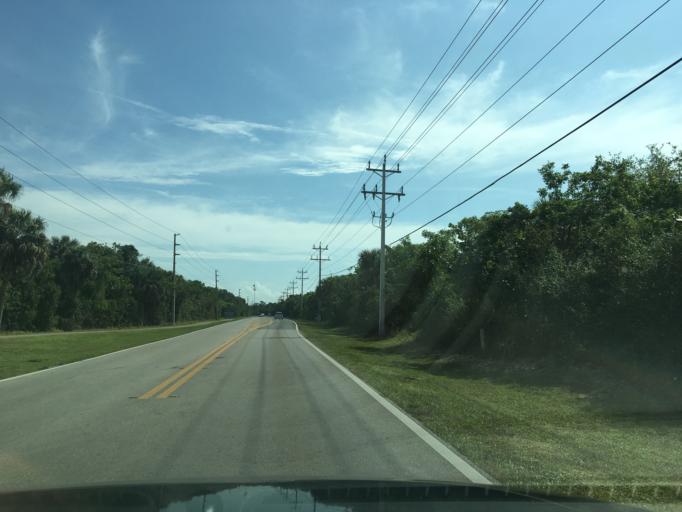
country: US
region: Florida
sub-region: Lee County
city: Saint James City
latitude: 26.4451
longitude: -82.1139
